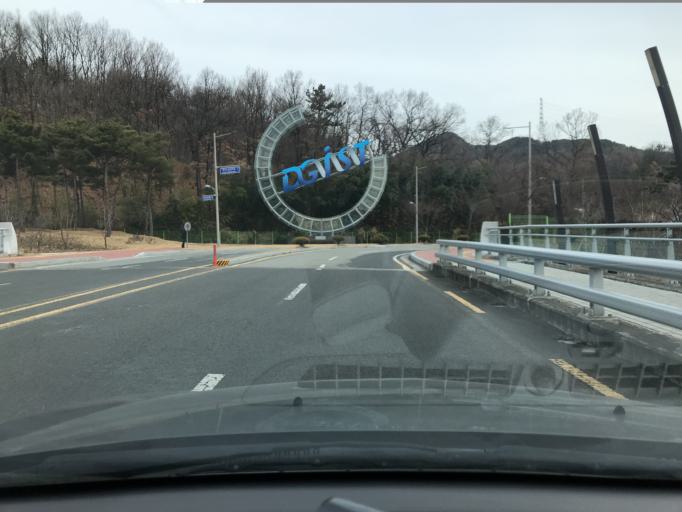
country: KR
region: Daegu
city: Hwawon
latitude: 35.6998
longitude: 128.4578
